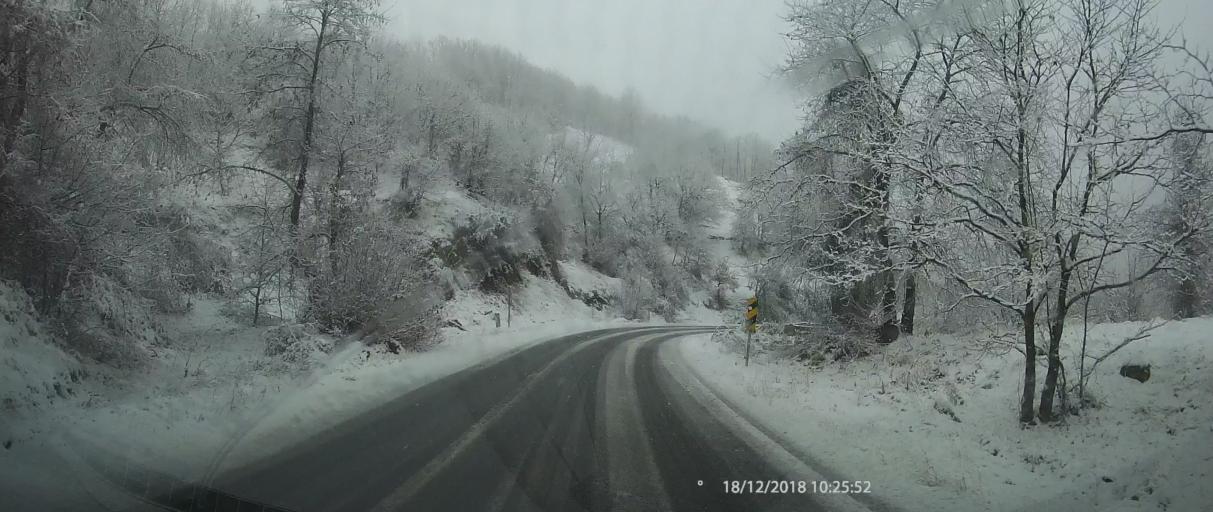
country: GR
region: Thessaly
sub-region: Nomos Larisis
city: Livadi
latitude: 40.1675
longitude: 22.2492
